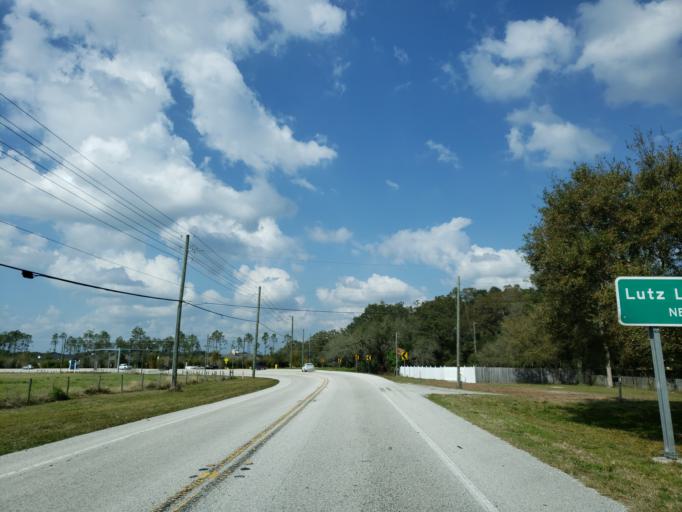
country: US
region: Florida
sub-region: Pasco County
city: Odessa
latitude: 28.1564
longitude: -82.5795
